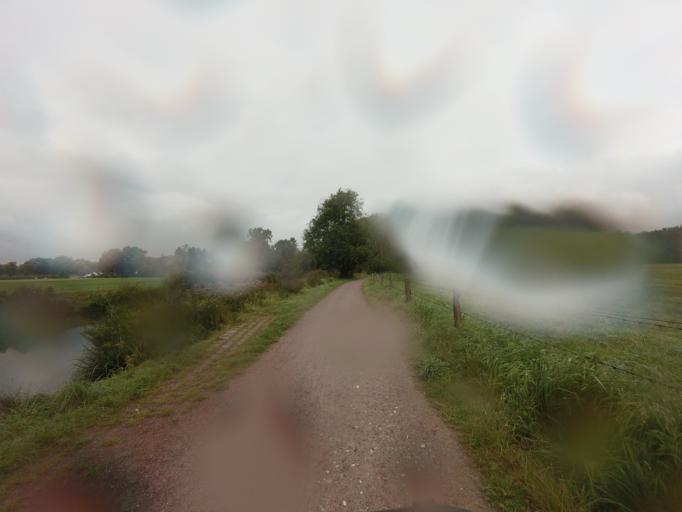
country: DE
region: North Rhine-Westphalia
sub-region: Regierungsbezirk Munster
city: Gronau
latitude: 52.1998
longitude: 7.0163
